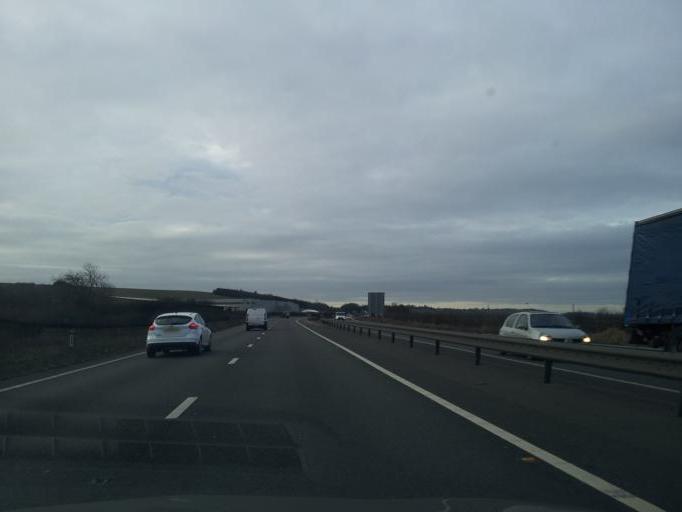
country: GB
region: England
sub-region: Lincolnshire
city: Great Gonerby
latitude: 52.9474
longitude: -0.6825
